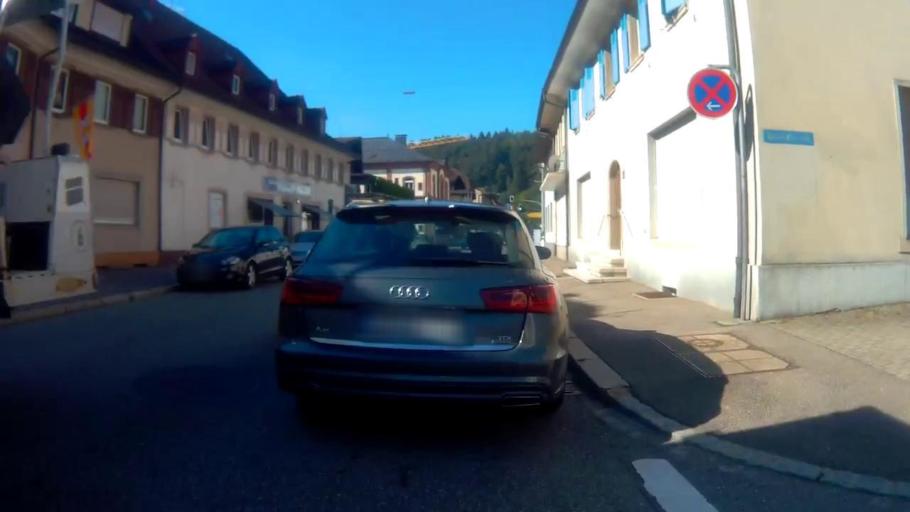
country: DE
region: Baden-Wuerttemberg
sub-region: Freiburg Region
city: Schonau im Schwarzwald
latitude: 47.7865
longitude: 7.8945
